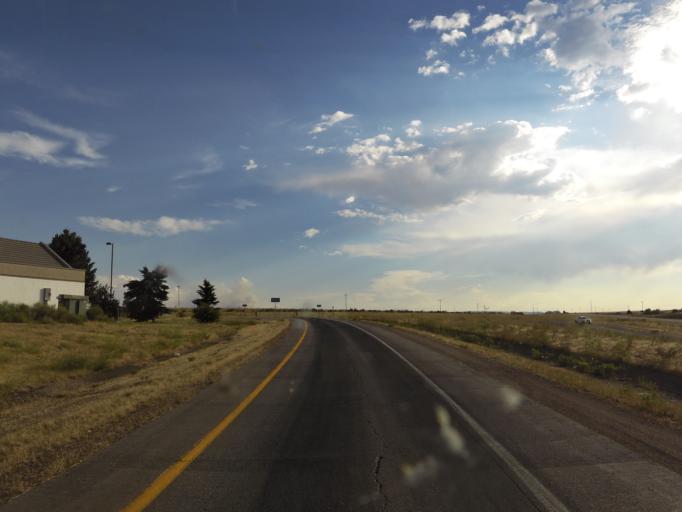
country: US
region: Idaho
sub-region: Power County
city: American Falls
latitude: 42.6143
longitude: -113.1458
